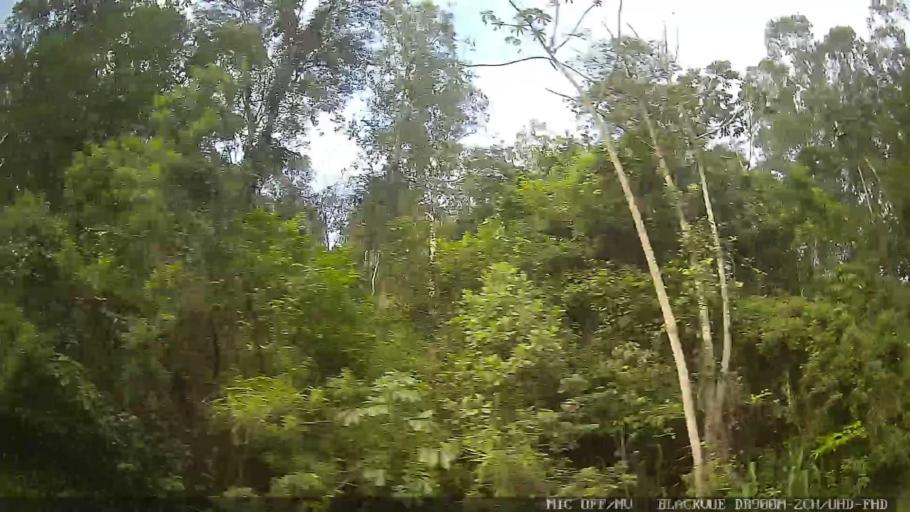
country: BR
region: Sao Paulo
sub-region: Amparo
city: Amparo
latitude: -22.6981
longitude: -46.7089
